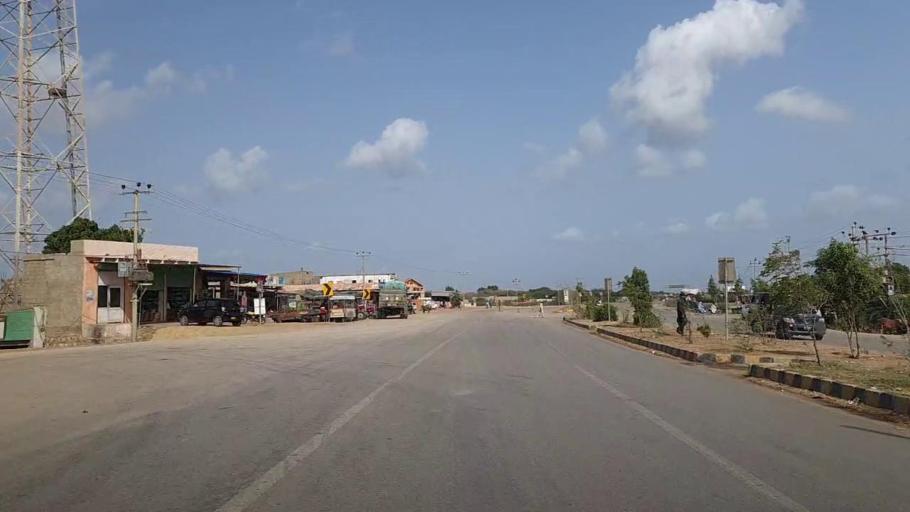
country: PK
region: Sindh
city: Gharo
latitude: 24.7401
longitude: 67.5950
